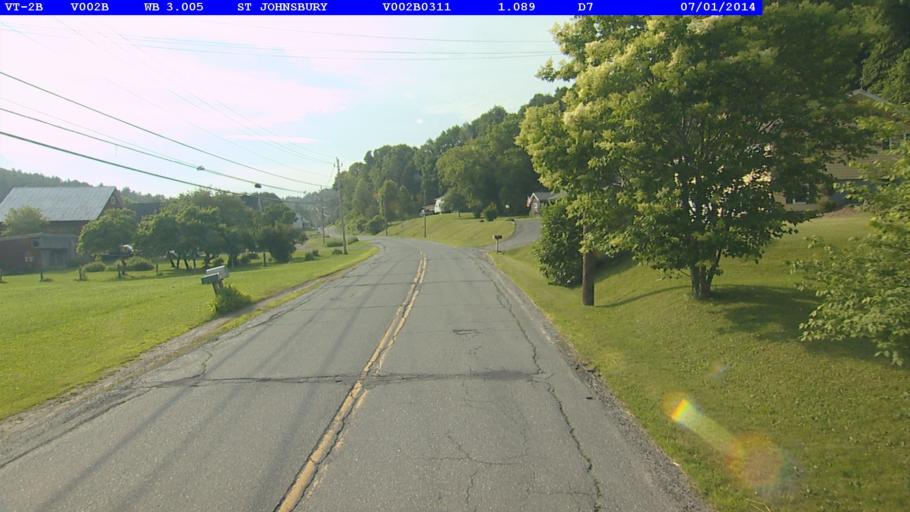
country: US
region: Vermont
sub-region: Caledonia County
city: St Johnsbury
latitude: 44.4228
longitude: -72.0374
